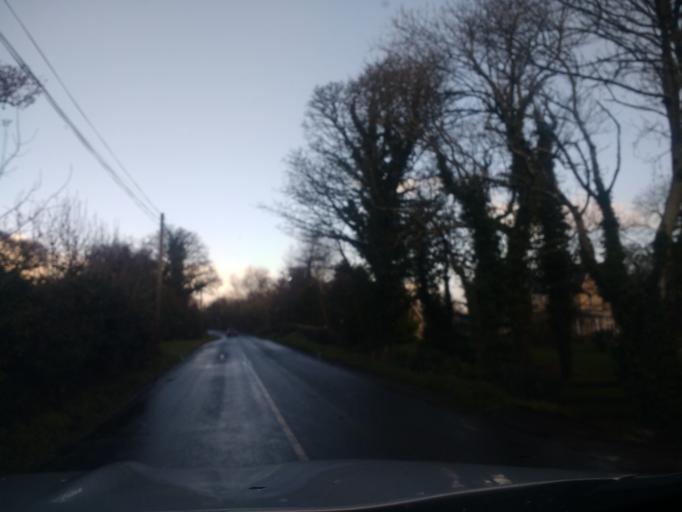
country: IE
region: Ulster
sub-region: County Donegal
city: Ramelton
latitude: 55.0456
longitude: -7.6441
